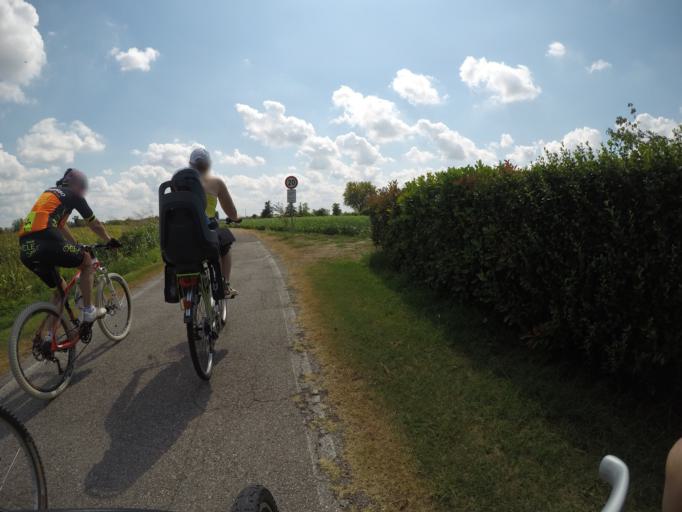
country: IT
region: Veneto
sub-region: Provincia di Rovigo
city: Lendinara
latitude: 45.0738
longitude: 11.6053
